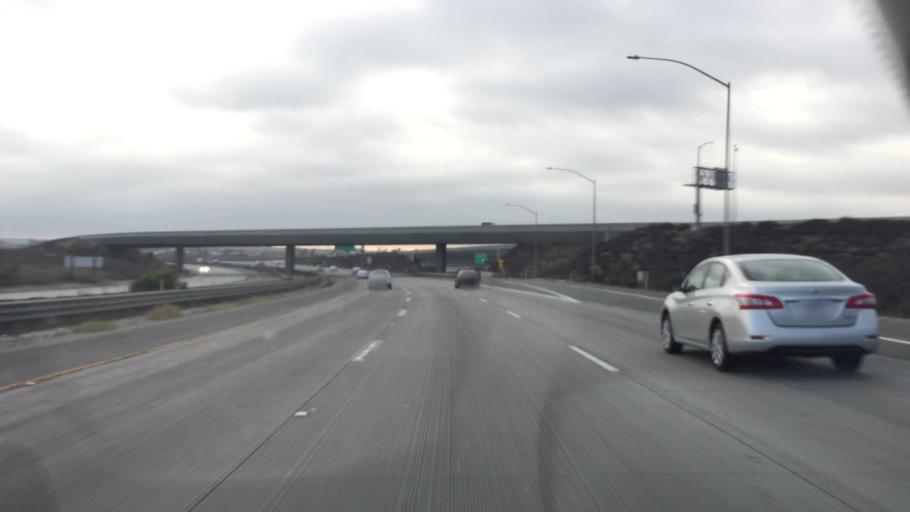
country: MX
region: Baja California
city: Tijuana
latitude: 32.5630
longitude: -116.9473
